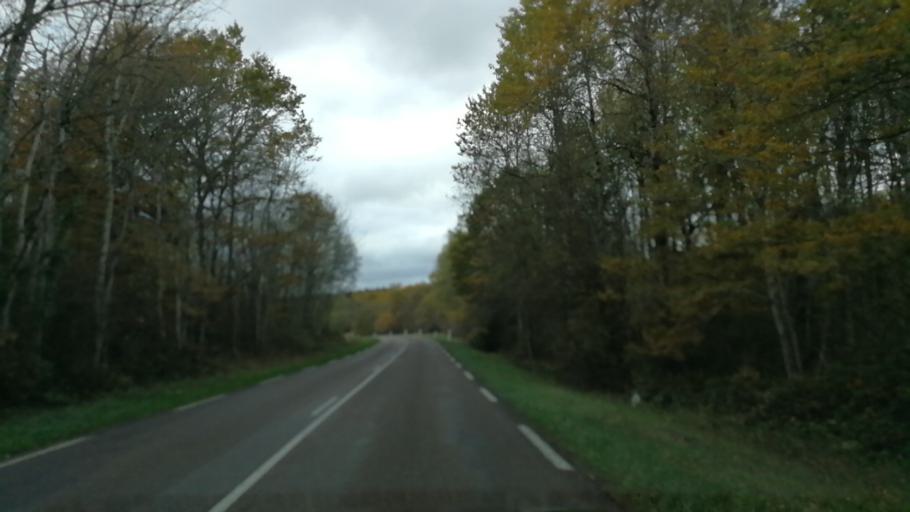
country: FR
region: Bourgogne
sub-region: Departement de la Cote-d'Or
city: Saulieu
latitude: 47.2593
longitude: 4.3206
